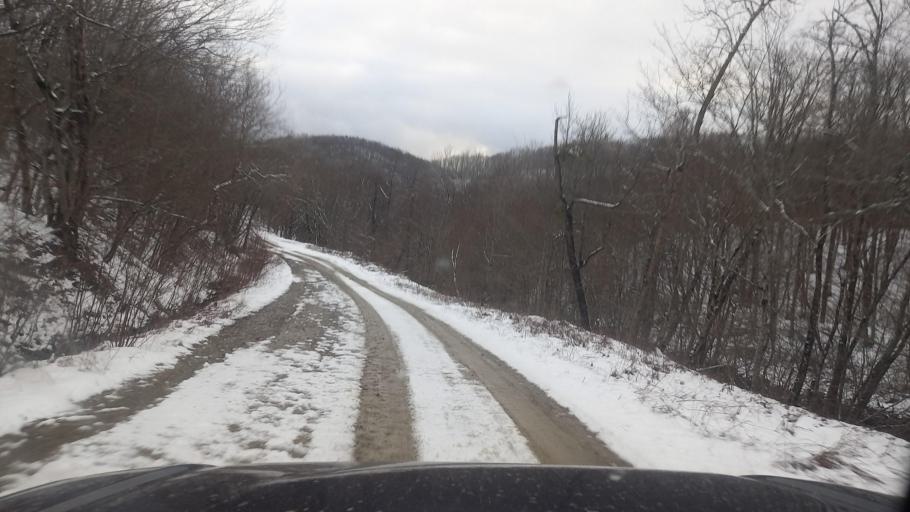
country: RU
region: Krasnodarskiy
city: Smolenskaya
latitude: 44.6619
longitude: 38.7641
